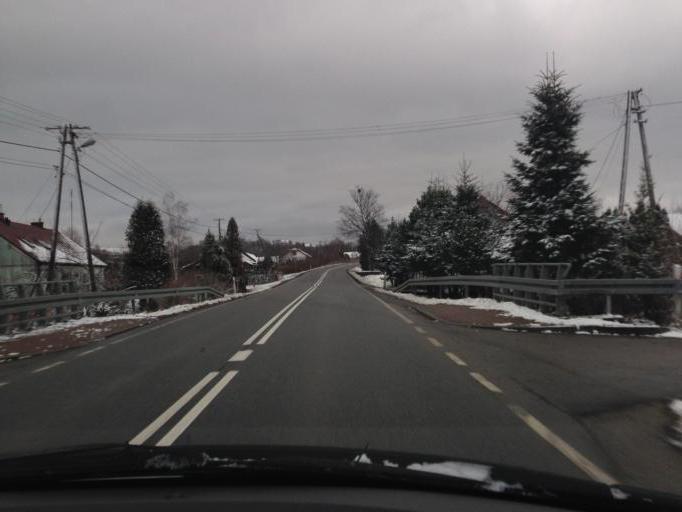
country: PL
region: Lesser Poland Voivodeship
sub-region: Powiat tarnowski
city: Siemiechow
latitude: 49.8509
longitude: 20.9181
